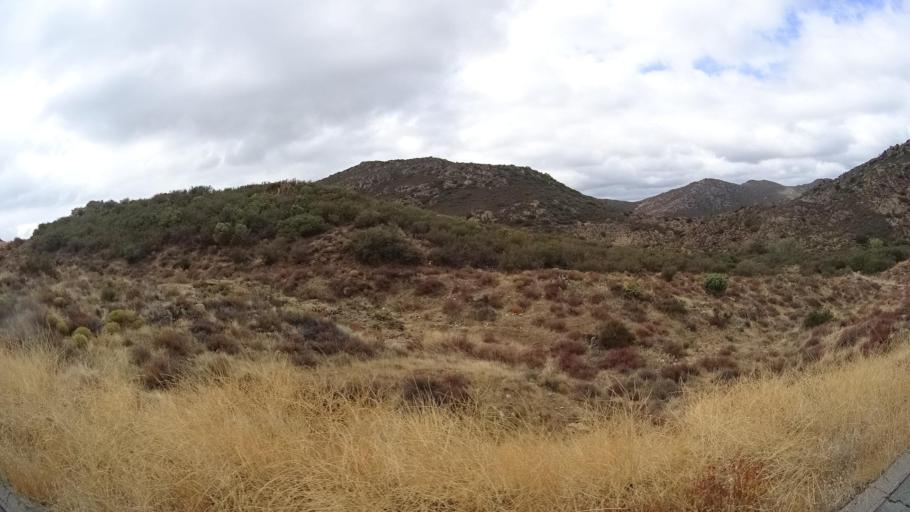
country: US
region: California
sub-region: San Diego County
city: Pine Valley
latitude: 32.7498
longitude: -116.4509
